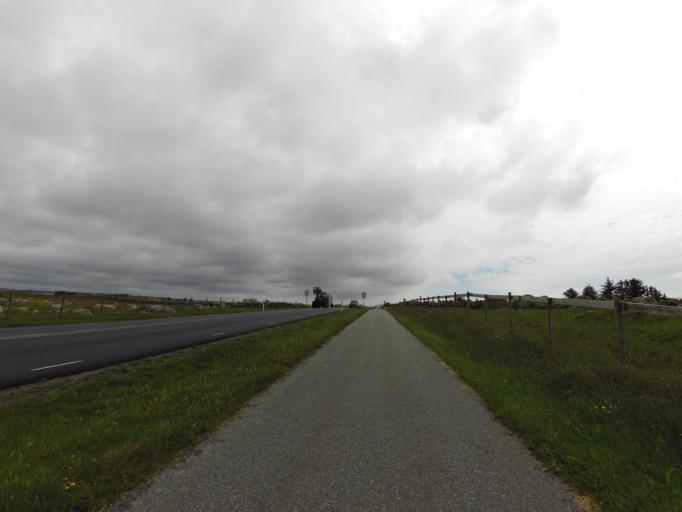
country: NO
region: Rogaland
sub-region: Ha
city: Naerbo
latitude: 58.6433
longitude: 5.6045
